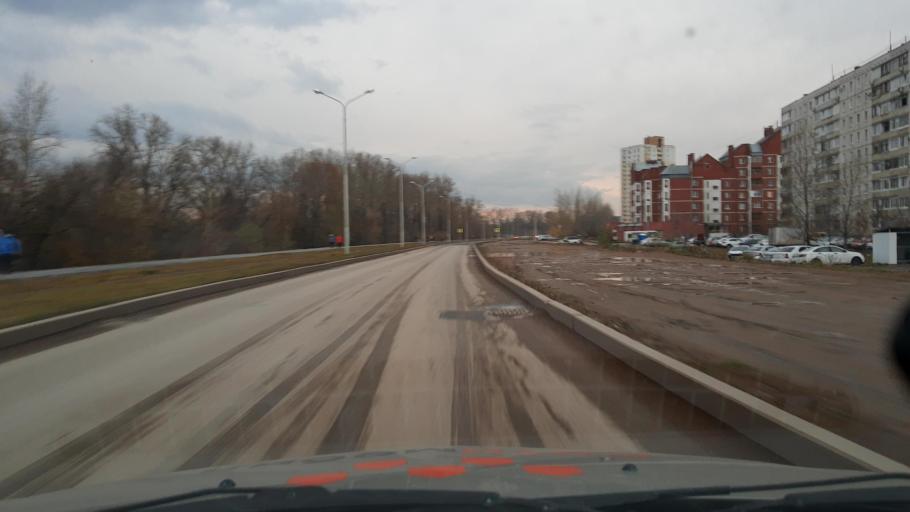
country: RU
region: Bashkortostan
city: Ufa
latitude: 54.7685
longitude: 56.0833
